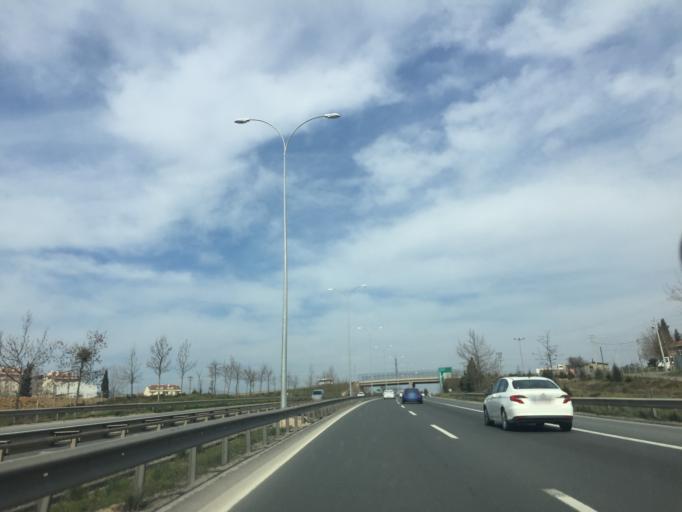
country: TR
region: Kocaeli
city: Balcik
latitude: 40.8553
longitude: 29.3758
